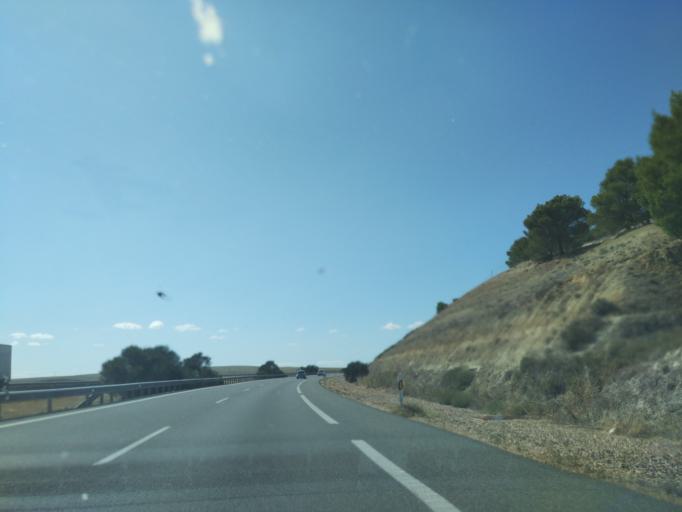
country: ES
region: Castille and Leon
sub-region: Provincia de Valladolid
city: Marzales
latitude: 41.6093
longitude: -5.1473
